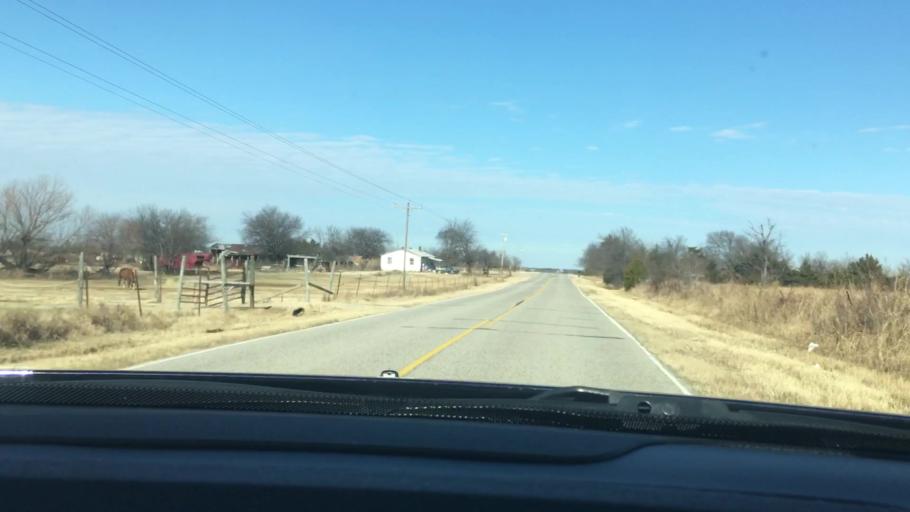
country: US
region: Oklahoma
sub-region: Garvin County
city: Wynnewood
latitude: 34.7042
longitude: -97.1254
